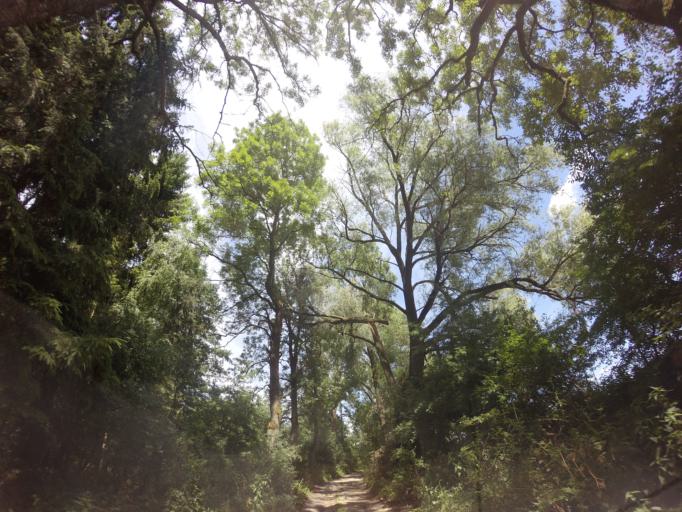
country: PL
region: West Pomeranian Voivodeship
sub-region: Powiat choszczenski
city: Recz
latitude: 53.2709
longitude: 15.5317
